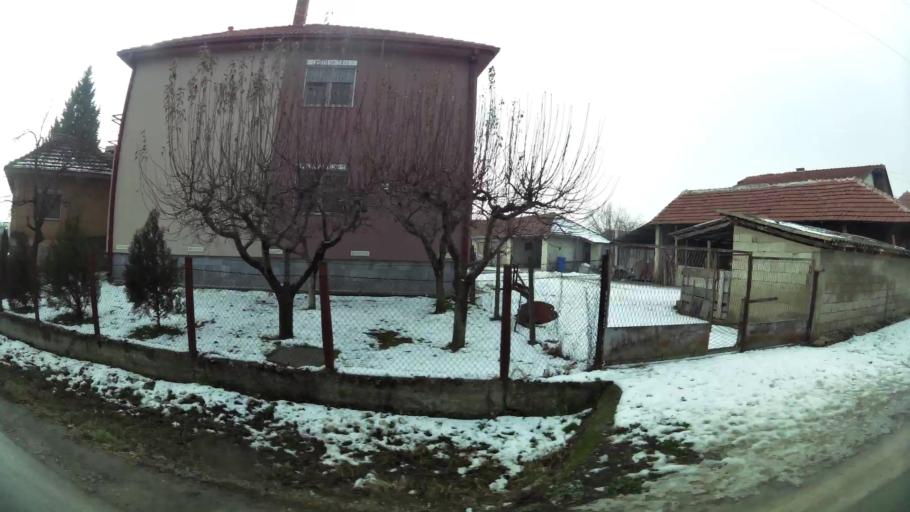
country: MK
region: Ilinden
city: Ilinden
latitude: 41.9940
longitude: 21.5813
